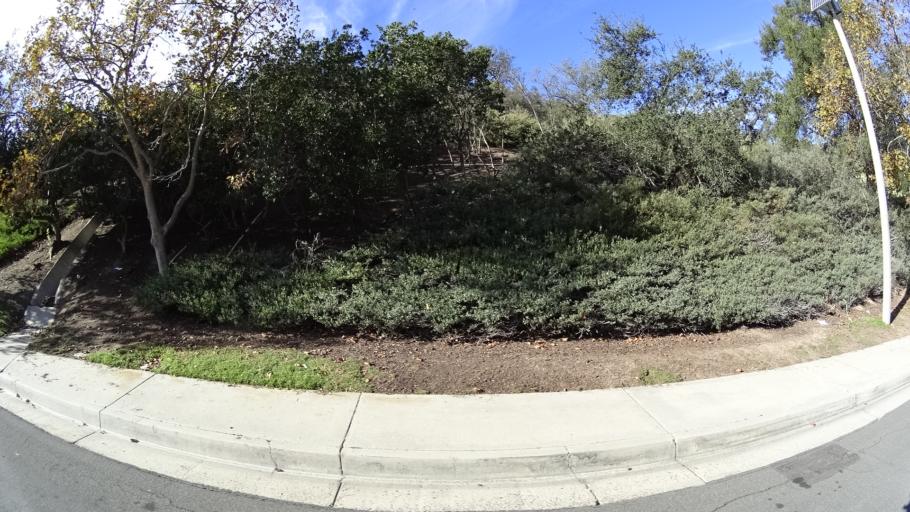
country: US
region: California
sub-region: Orange County
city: Portola Hills
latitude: 33.6894
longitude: -117.6273
